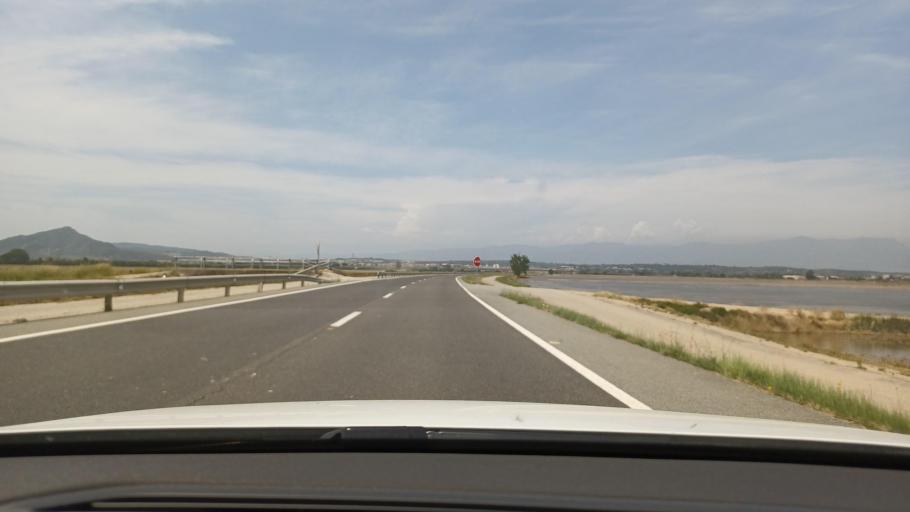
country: ES
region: Catalonia
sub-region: Provincia de Tarragona
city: Amposta
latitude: 40.7122
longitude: 0.6141
